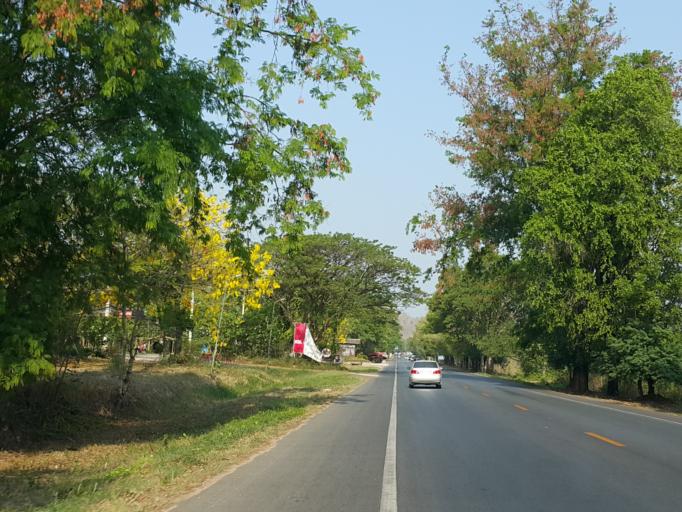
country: TH
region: Kanchanaburi
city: Sai Yok
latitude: 14.0898
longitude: 99.2897
